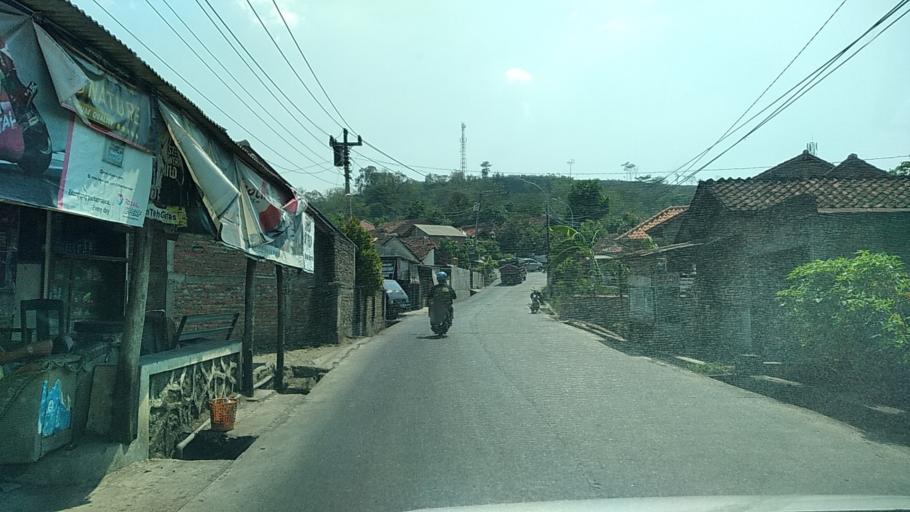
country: ID
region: Central Java
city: Semarang
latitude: -7.0168
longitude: 110.3591
